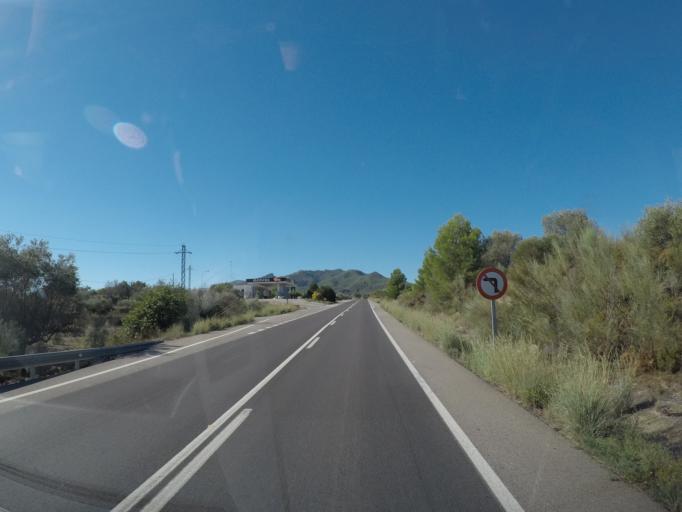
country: ES
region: Catalonia
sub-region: Provincia de Tarragona
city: Rasquera
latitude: 41.0139
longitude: 0.6109
